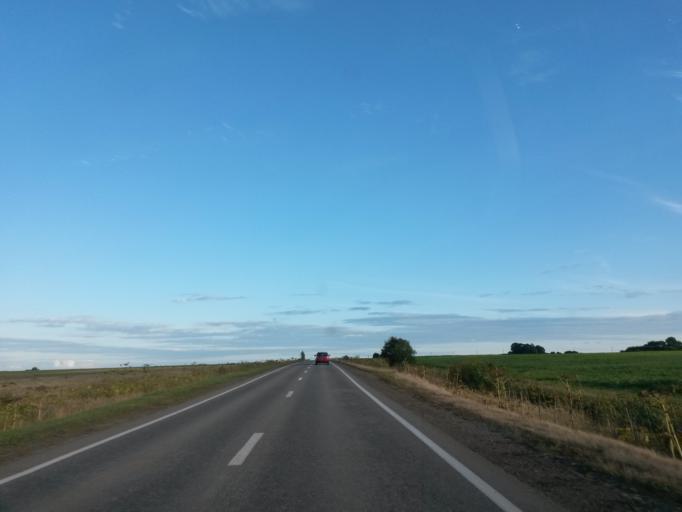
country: RU
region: Jaroslavl
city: Yaroslavl
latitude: 57.7651
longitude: 39.8612
